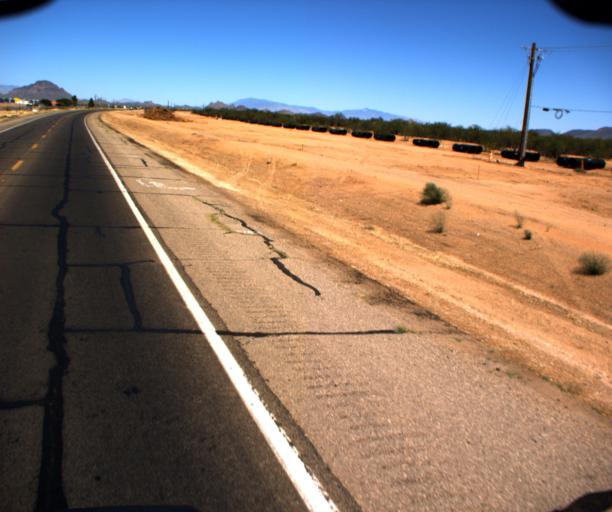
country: US
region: Arizona
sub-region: Pima County
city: Valencia West
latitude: 32.1313
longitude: -111.1802
